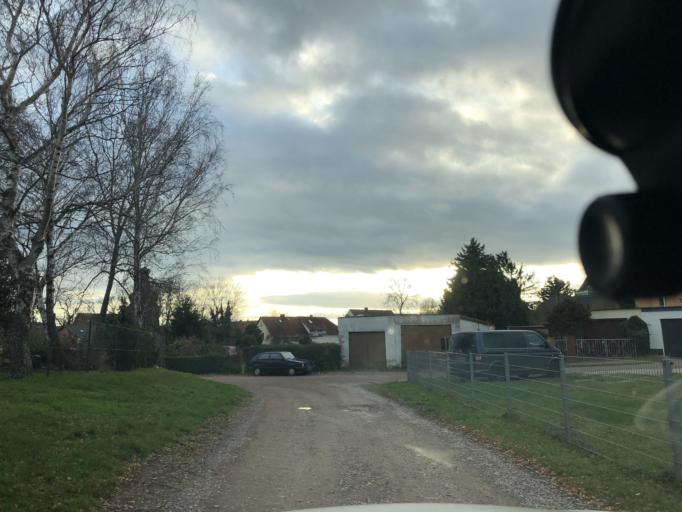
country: DE
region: Saxony-Anhalt
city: Zscherben
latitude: 51.4699
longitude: 11.8713
